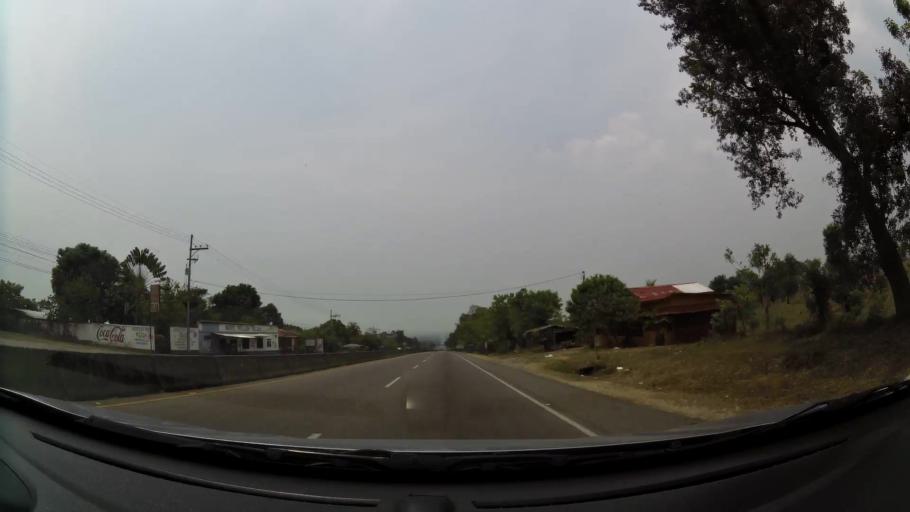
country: HN
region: Cortes
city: Oropendolas
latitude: 15.0229
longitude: -87.9276
